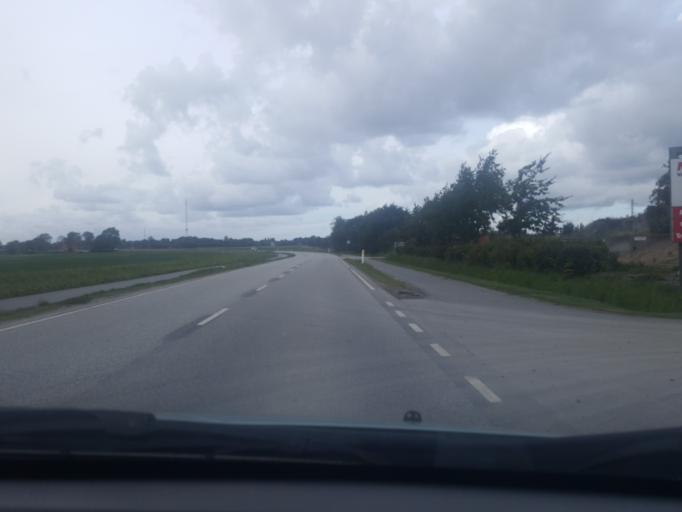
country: DK
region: Zealand
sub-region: Guldborgsund Kommune
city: Nykobing Falster
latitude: 54.6989
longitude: 11.9470
